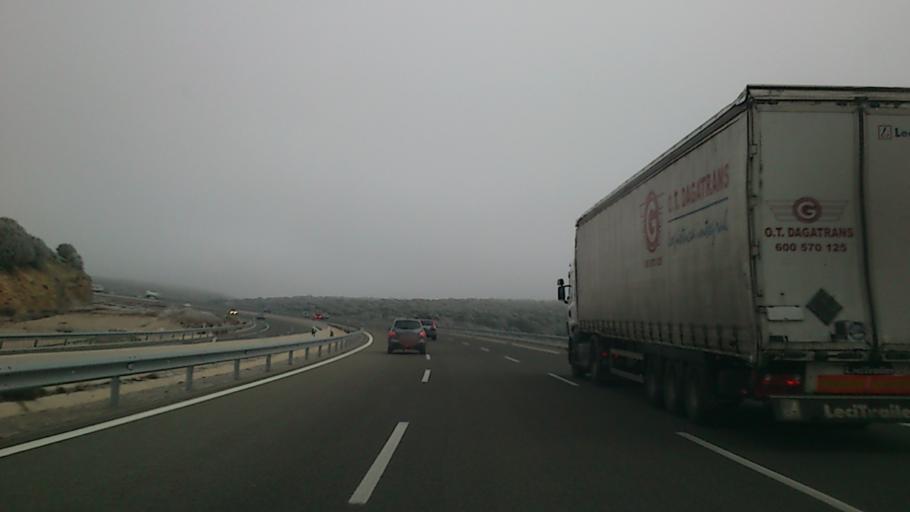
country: ES
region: Castille-La Mancha
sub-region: Provincia de Guadalajara
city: Sauca
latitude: 41.0184
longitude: -2.5233
